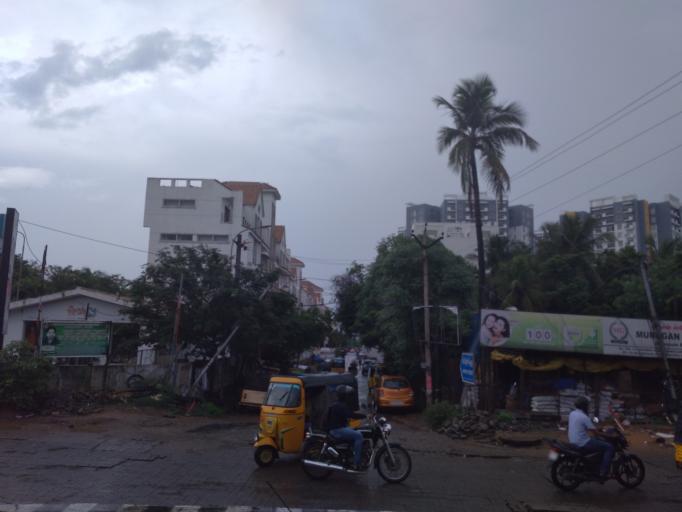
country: IN
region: Tamil Nadu
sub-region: Kancheepuram
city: Injambakkam
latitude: 12.9041
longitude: 80.2280
